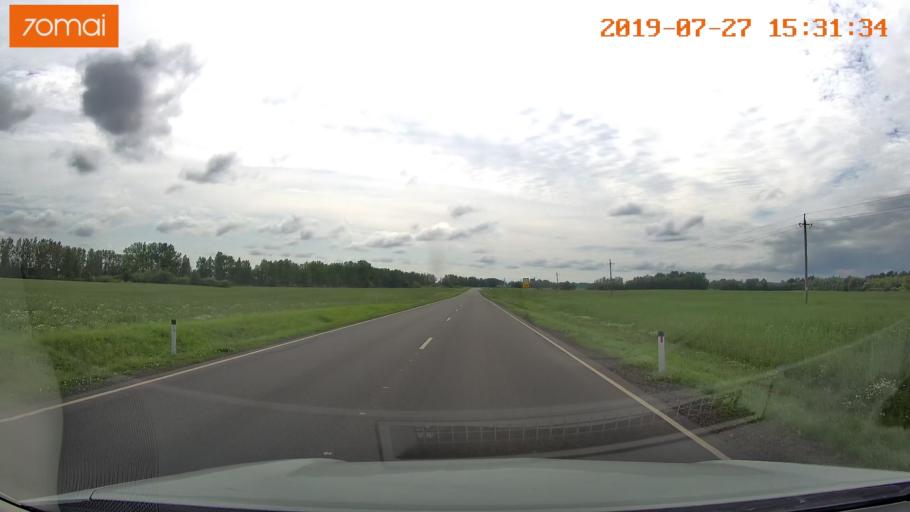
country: RU
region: Kaliningrad
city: Nesterov
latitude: 54.6222
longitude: 22.4899
